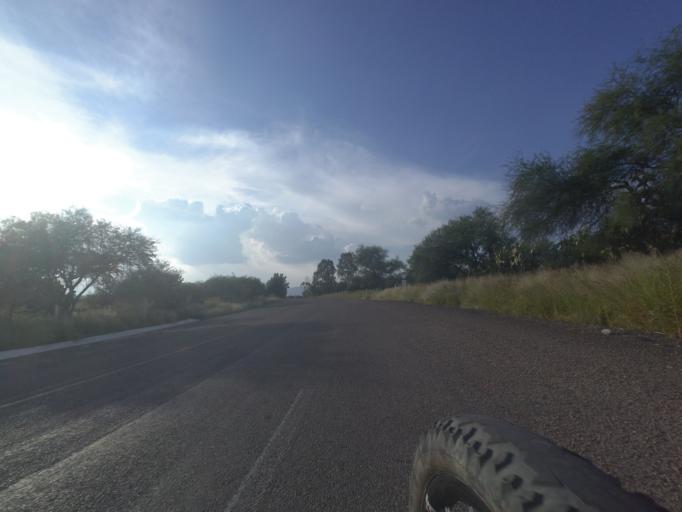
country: MX
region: Aguascalientes
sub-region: Aguascalientes
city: Penuelas (El Cienegal)
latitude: 21.7639
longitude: -102.3521
